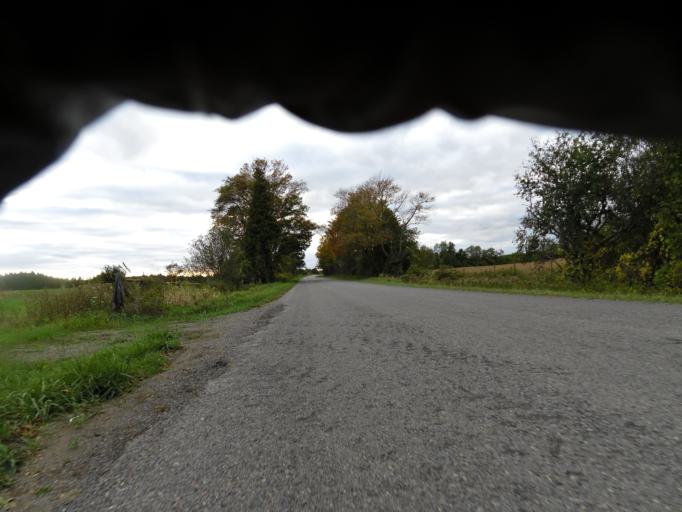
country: CA
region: Ontario
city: Cobourg
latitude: 43.9791
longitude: -77.9276
